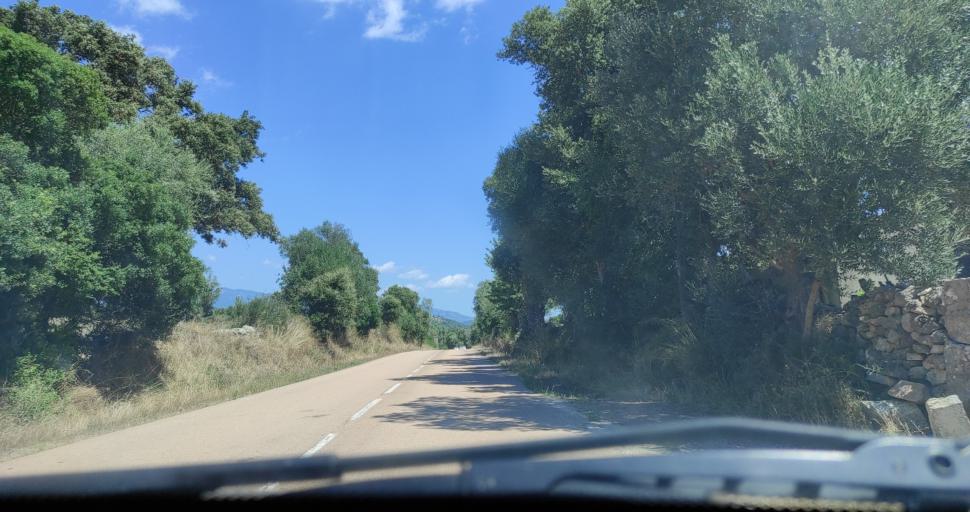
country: FR
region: Corsica
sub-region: Departement de la Corse-du-Sud
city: Porto-Vecchio
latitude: 41.5423
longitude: 9.1786
